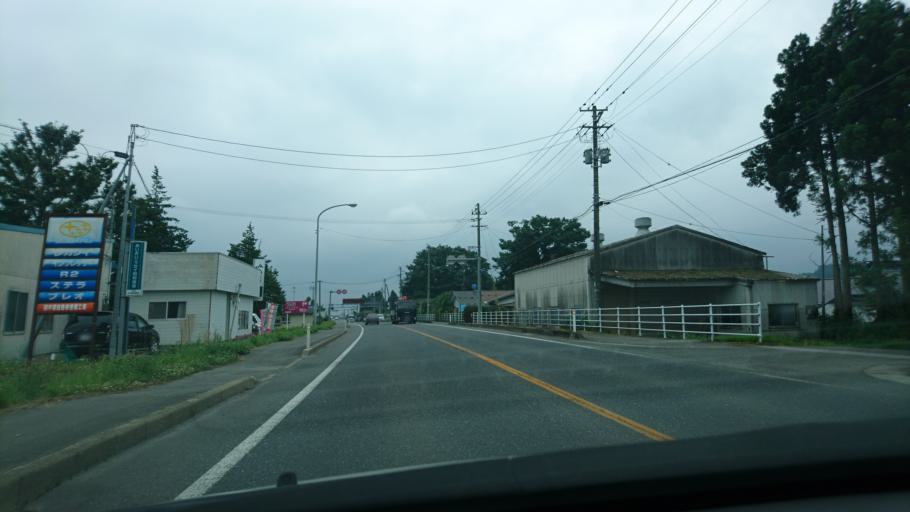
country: JP
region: Miyagi
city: Furukawa
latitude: 38.6822
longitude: 140.8572
